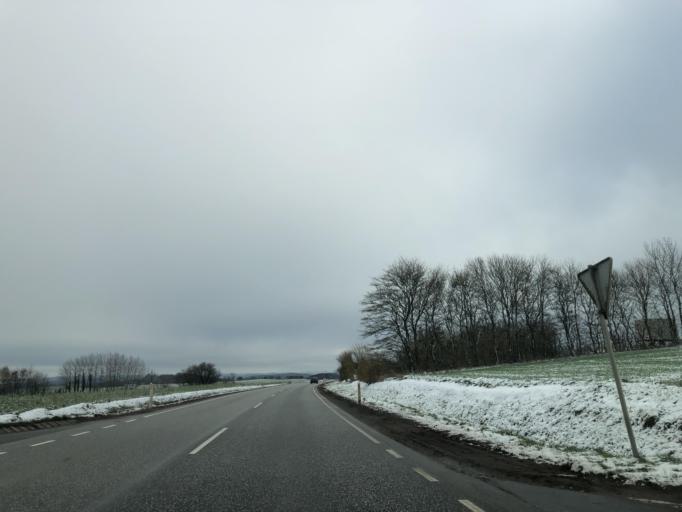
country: DK
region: Central Jutland
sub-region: Hedensted Kommune
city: Hedensted
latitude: 55.8960
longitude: 9.7199
